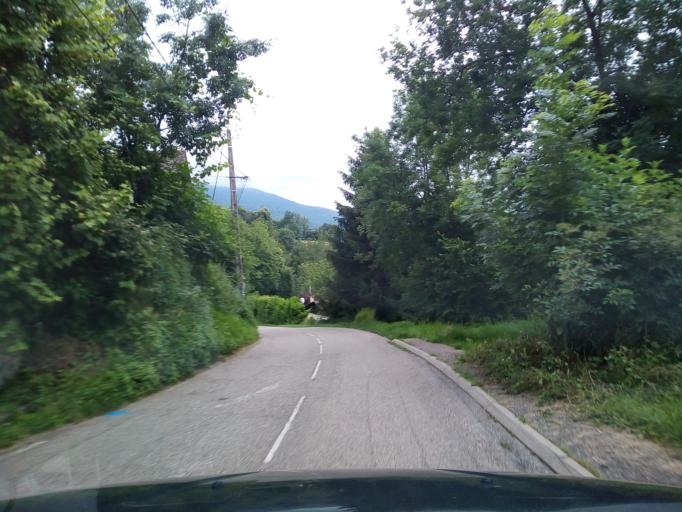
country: FR
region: Rhone-Alpes
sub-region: Departement de l'Isere
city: Vaulnaveys-le-Haut
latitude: 45.1343
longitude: 5.8359
